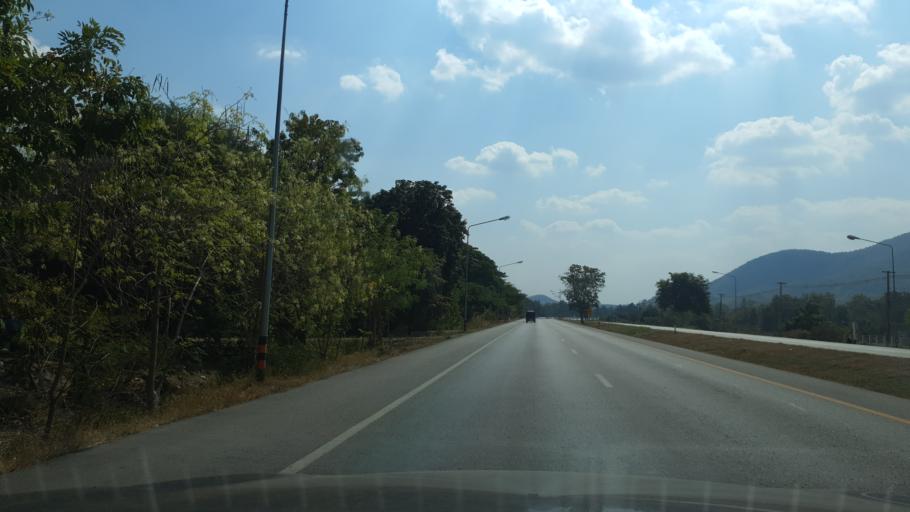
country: TH
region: Lampang
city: Mae Phrik
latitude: 17.3581
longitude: 99.1482
